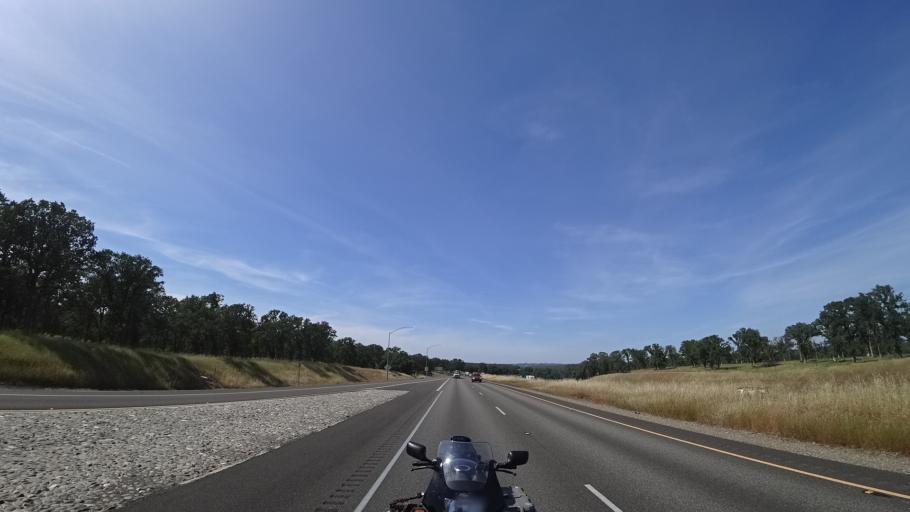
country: US
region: California
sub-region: Tehama County
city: Red Bluff
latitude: 40.2208
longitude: -122.2528
